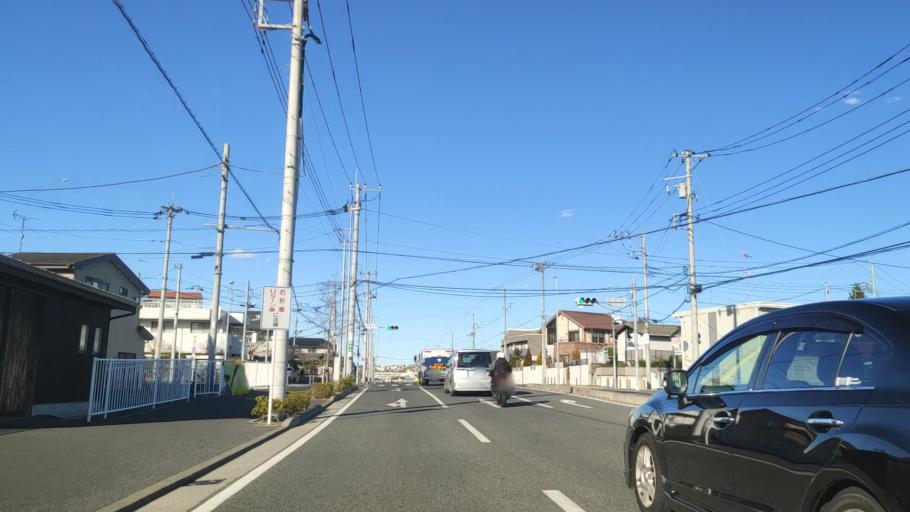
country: JP
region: Tokyo
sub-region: Machida-shi
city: Machida
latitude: 35.5197
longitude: 139.5443
